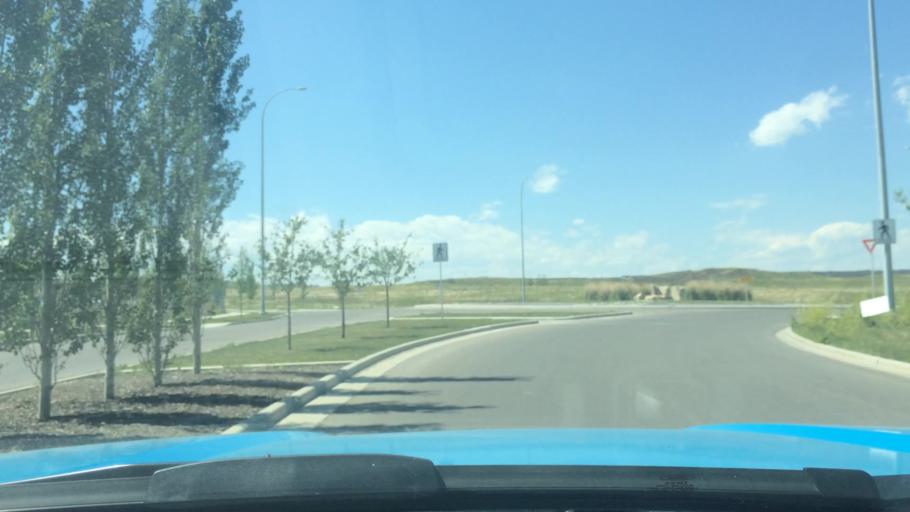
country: CA
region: Alberta
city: Calgary
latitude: 51.1709
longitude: -114.1441
